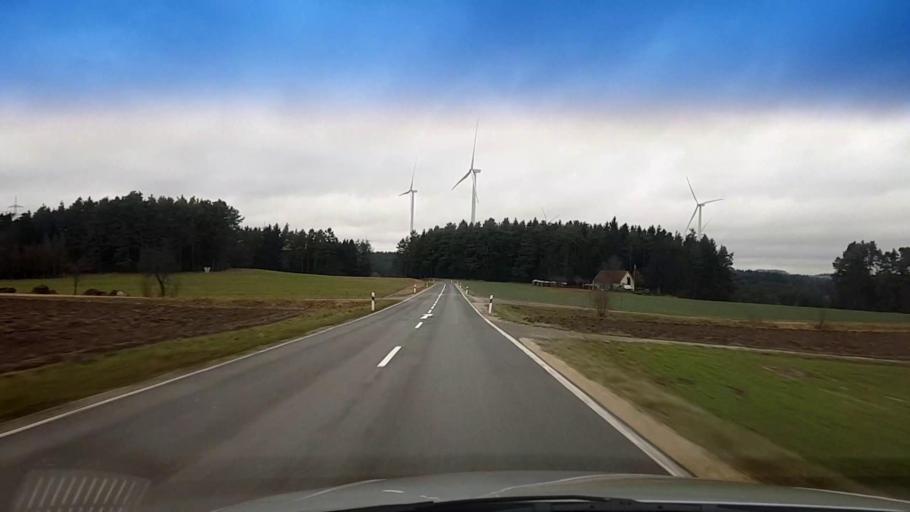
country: DE
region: Bavaria
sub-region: Upper Franconia
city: Wattendorf
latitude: 50.0084
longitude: 11.1334
